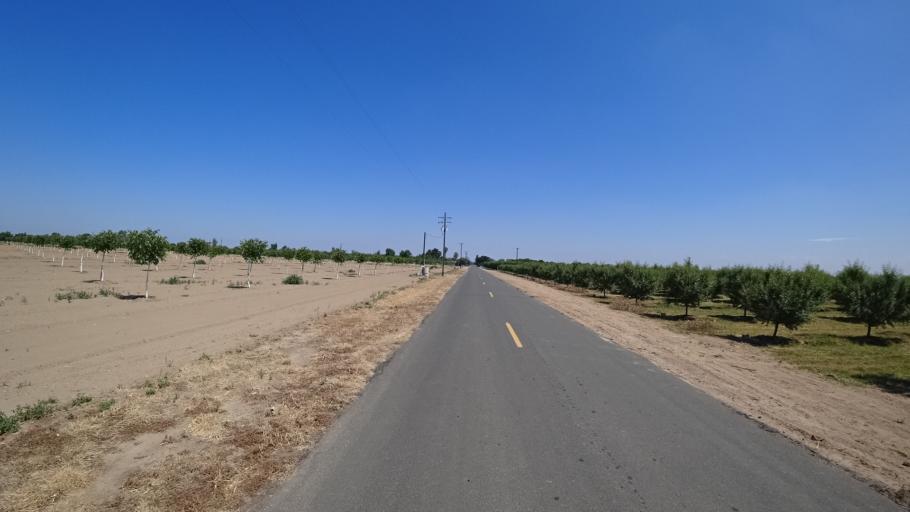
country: US
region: California
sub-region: Fresno County
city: Kingsburg
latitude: 36.4620
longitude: -119.5734
